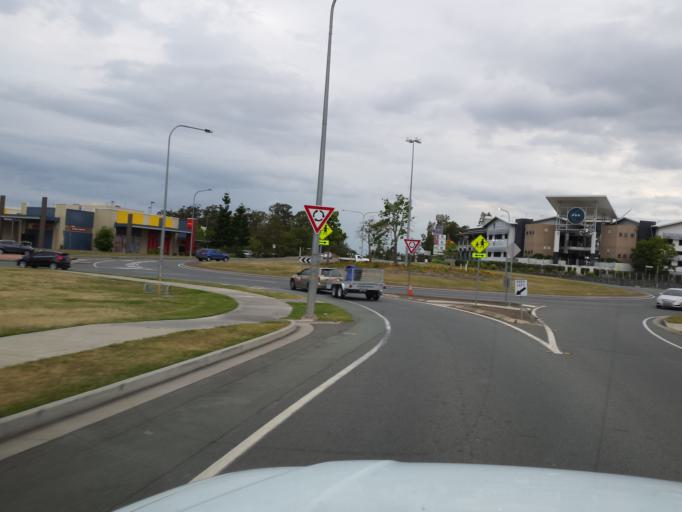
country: AU
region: Queensland
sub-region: Gold Coast
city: Oxenford
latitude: -27.8519
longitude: 153.2989
